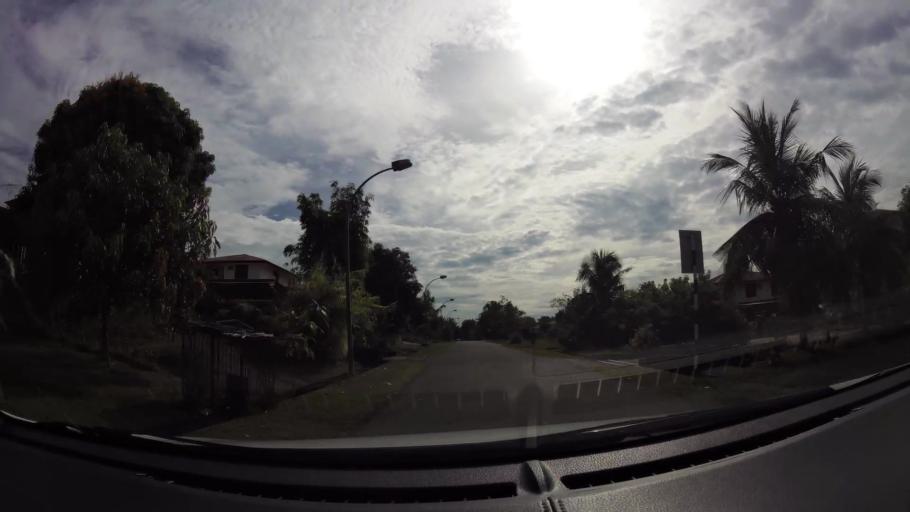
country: BN
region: Brunei and Muara
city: Bandar Seri Begawan
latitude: 4.8949
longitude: 114.8879
